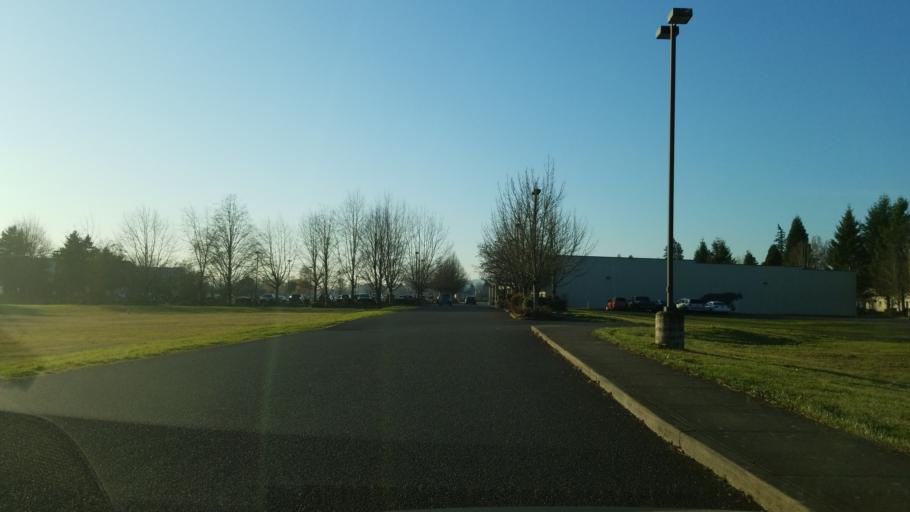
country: US
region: Washington
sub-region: Clark County
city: Washougal
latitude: 45.5768
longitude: -122.3371
